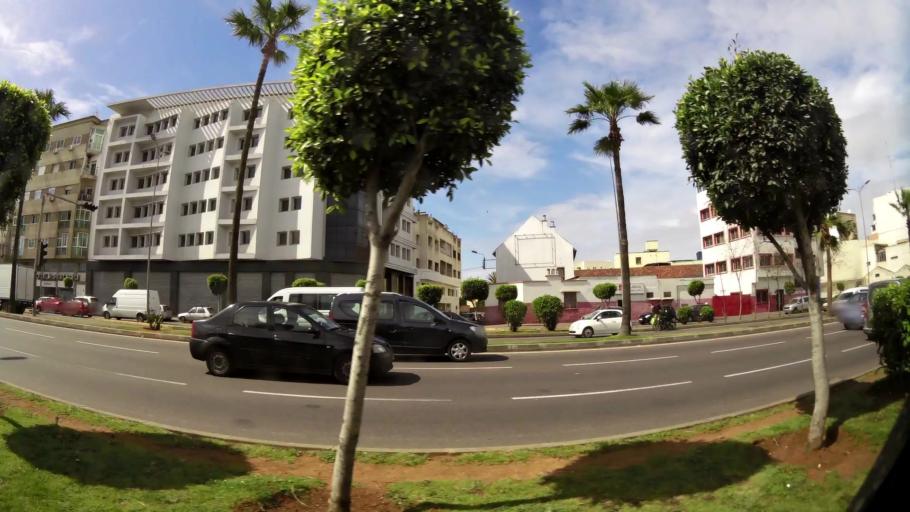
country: MA
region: Grand Casablanca
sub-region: Casablanca
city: Casablanca
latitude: 33.5828
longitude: -7.5951
